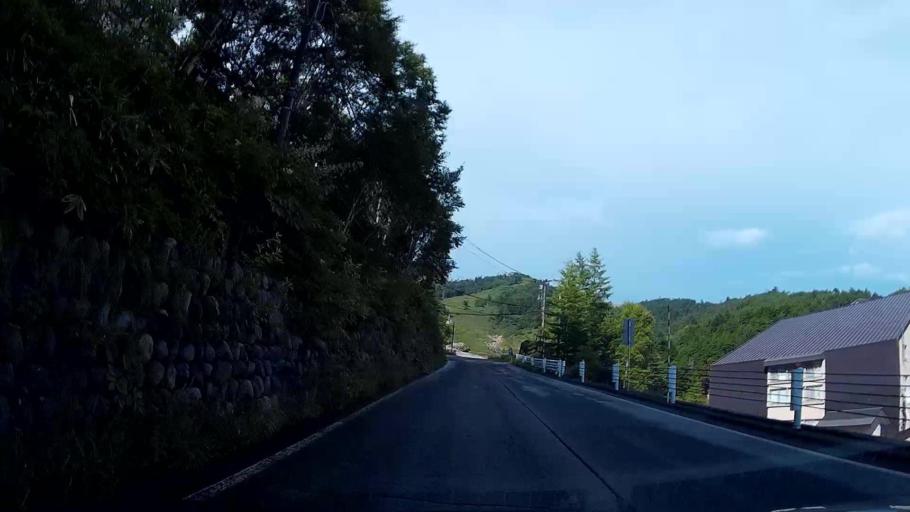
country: JP
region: Nagano
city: Nakano
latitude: 36.6360
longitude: 138.5082
